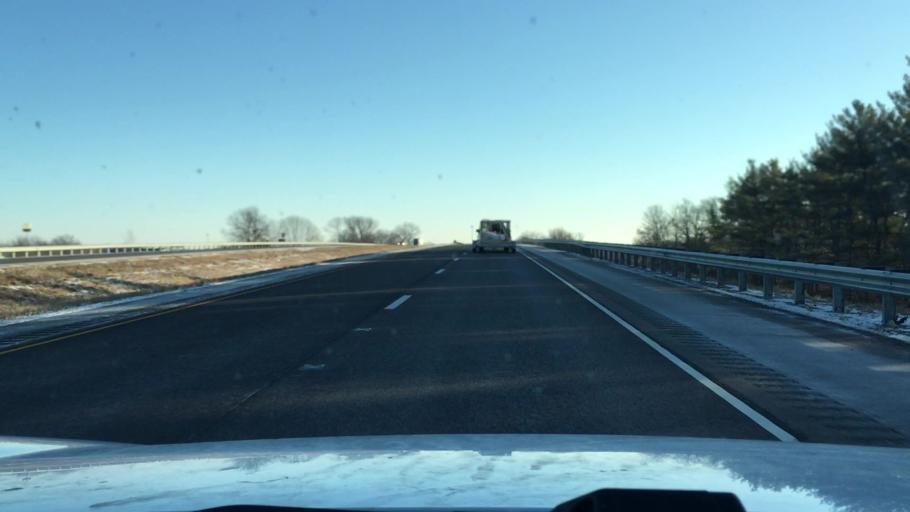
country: US
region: Illinois
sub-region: Effingham County
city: Altamont
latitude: 39.0421
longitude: -88.7548
